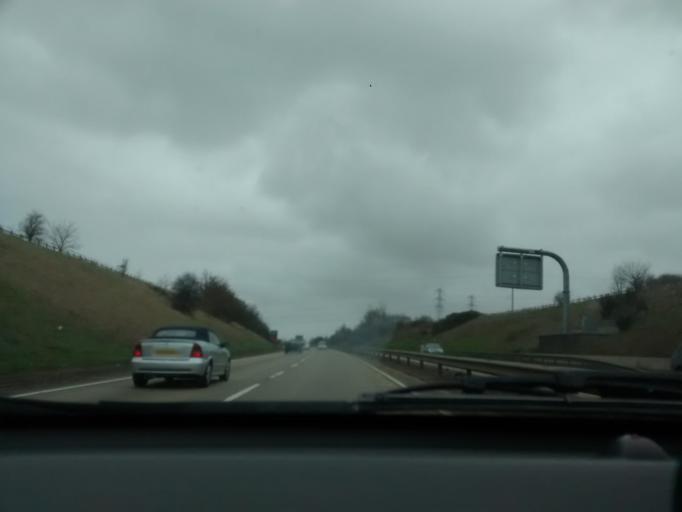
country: GB
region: England
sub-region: Suffolk
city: Bramford
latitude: 52.0486
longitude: 1.0972
